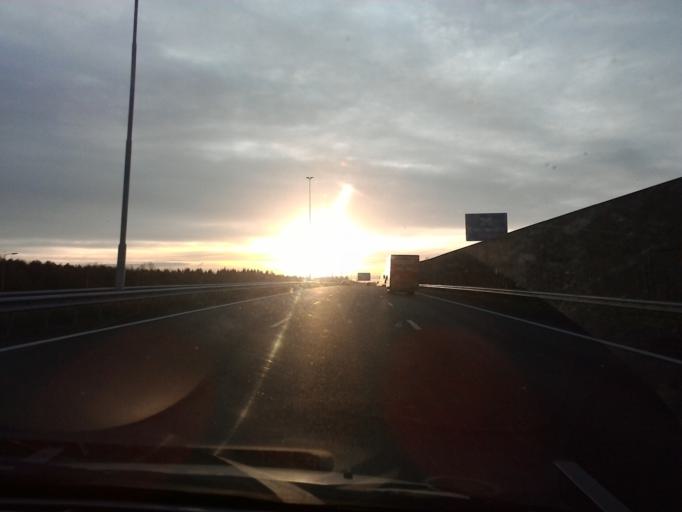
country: NL
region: North Brabant
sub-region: Gemeente Best
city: Best
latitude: 51.5075
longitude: 5.4110
